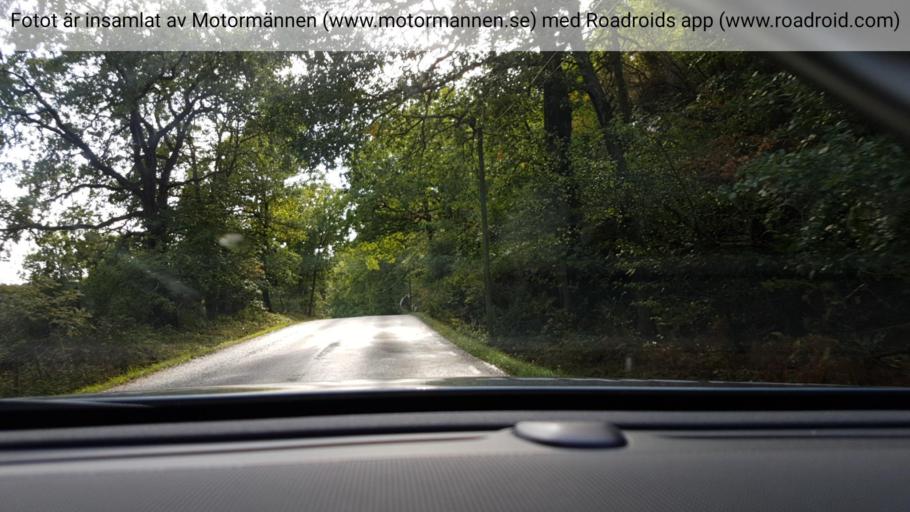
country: SE
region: Vaestra Goetaland
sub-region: Tjorns Kommun
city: Myggenas
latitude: 58.0563
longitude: 11.6778
